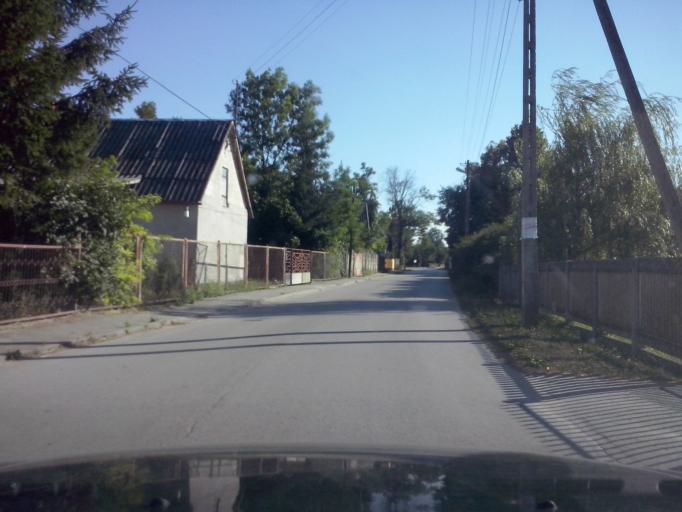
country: PL
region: Swietokrzyskie
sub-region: Powiat kielecki
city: Chmielnik
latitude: 50.5796
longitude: 20.7072
